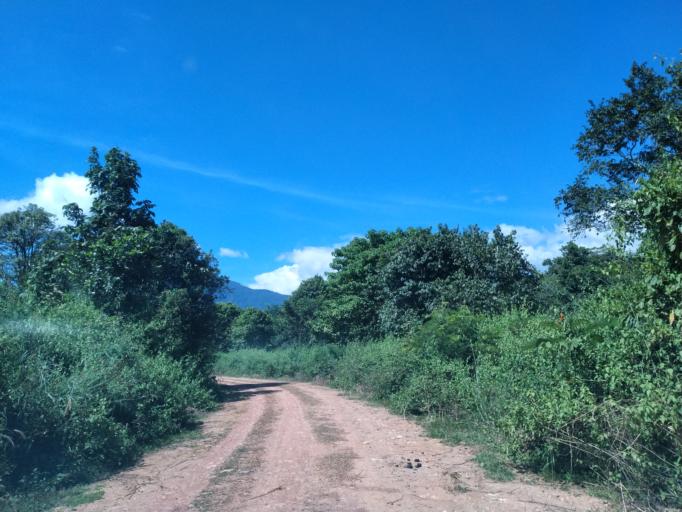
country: LA
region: Vientiane
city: Muang Phon-Hong
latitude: 18.6197
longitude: 102.8653
